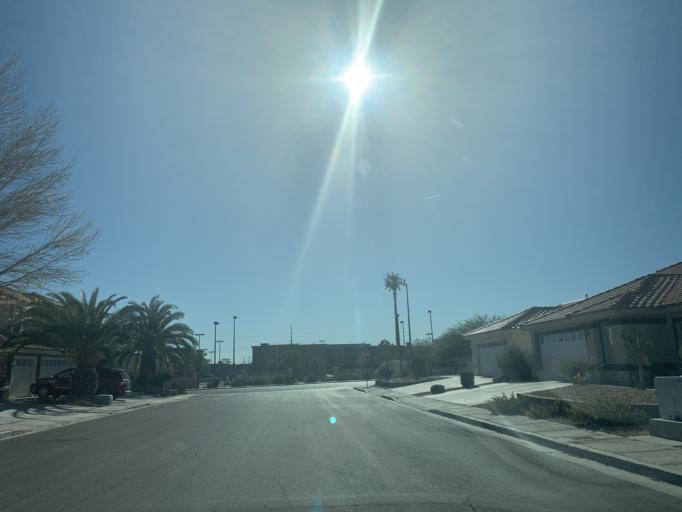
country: US
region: Nevada
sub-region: Clark County
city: Summerlin South
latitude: 36.1173
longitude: -115.2943
